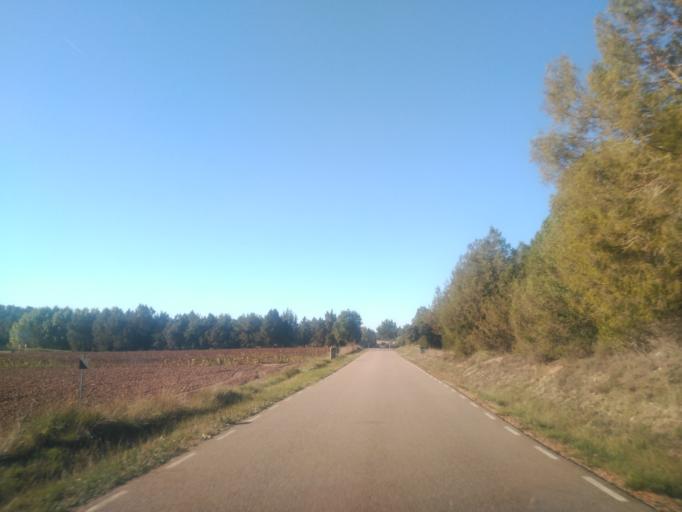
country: ES
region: Castille and Leon
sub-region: Provincia de Burgos
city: Brazacorta
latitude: 41.7034
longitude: -3.3929
